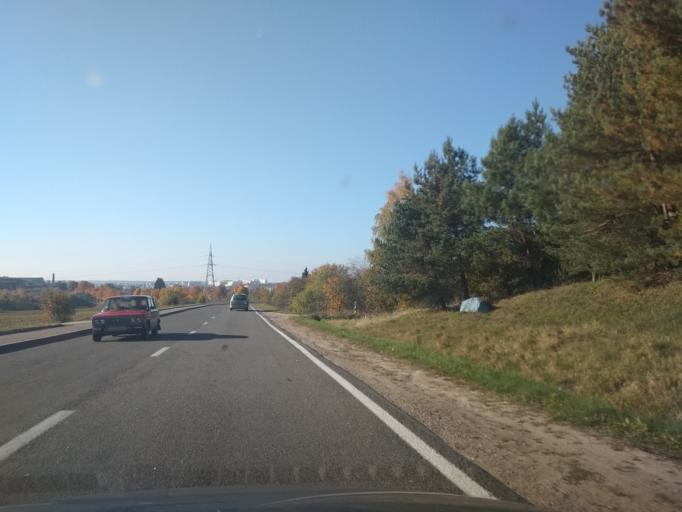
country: BY
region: Grodnenskaya
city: Vawkavysk
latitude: 53.1551
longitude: 24.4932
